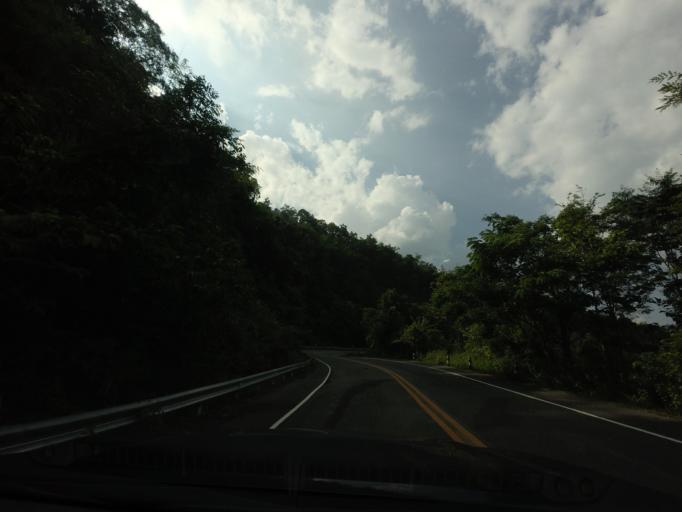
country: TH
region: Nan
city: Na Noi
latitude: 18.2865
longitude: 100.9288
